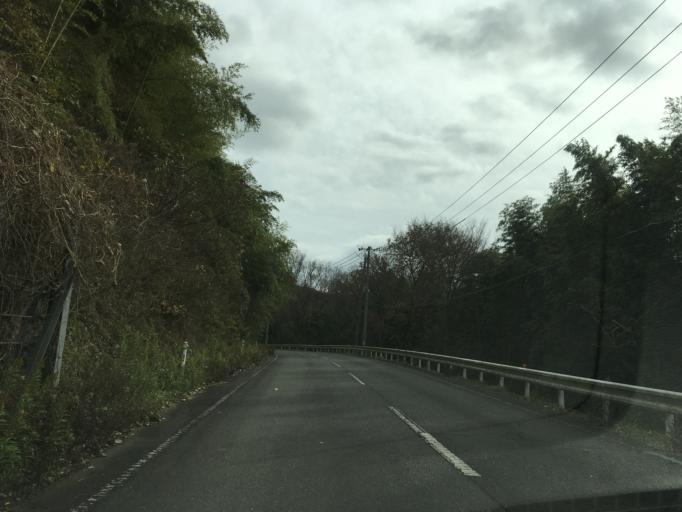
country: JP
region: Iwate
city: Ichinoseki
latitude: 38.7897
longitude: 141.2610
